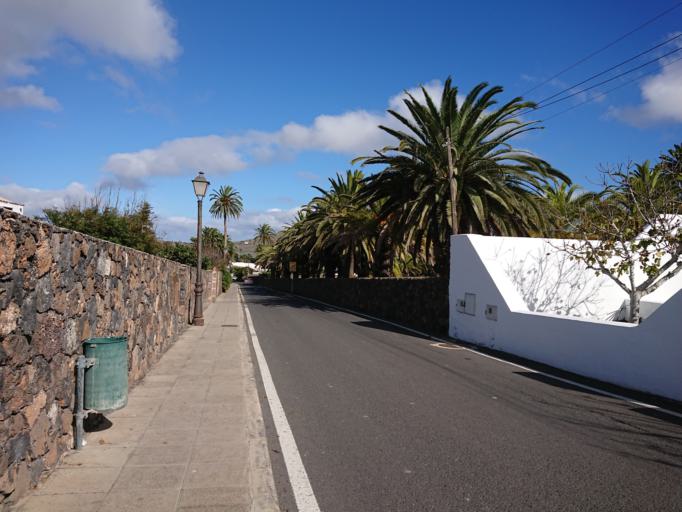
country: ES
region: Canary Islands
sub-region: Provincia de Las Palmas
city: Haria
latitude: 29.1419
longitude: -13.5048
